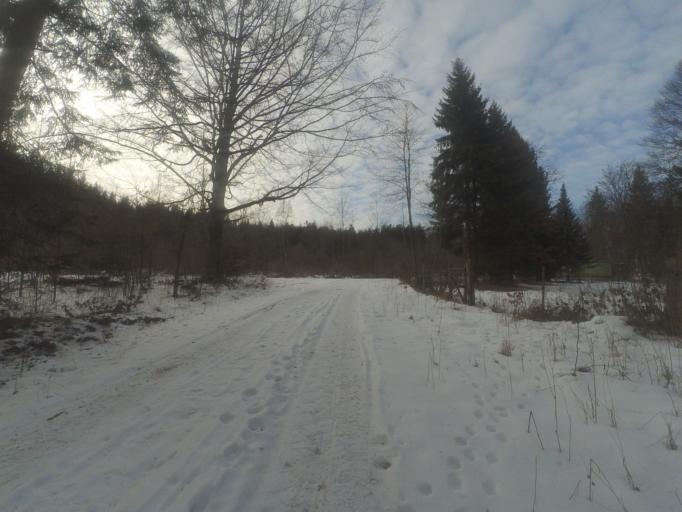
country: DE
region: Baden-Wuerttemberg
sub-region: Regierungsbezirk Stuttgart
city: Aalen
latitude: 48.8124
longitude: 10.0840
